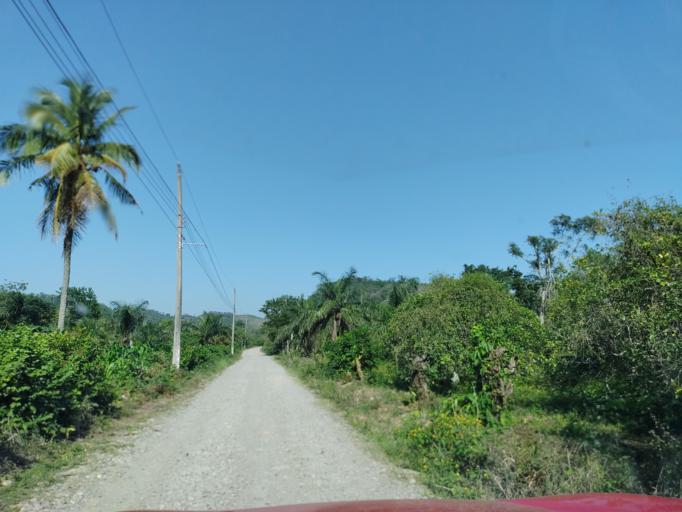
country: MX
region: Veracruz
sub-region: Papantla
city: Polutla
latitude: 20.4843
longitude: -97.1914
